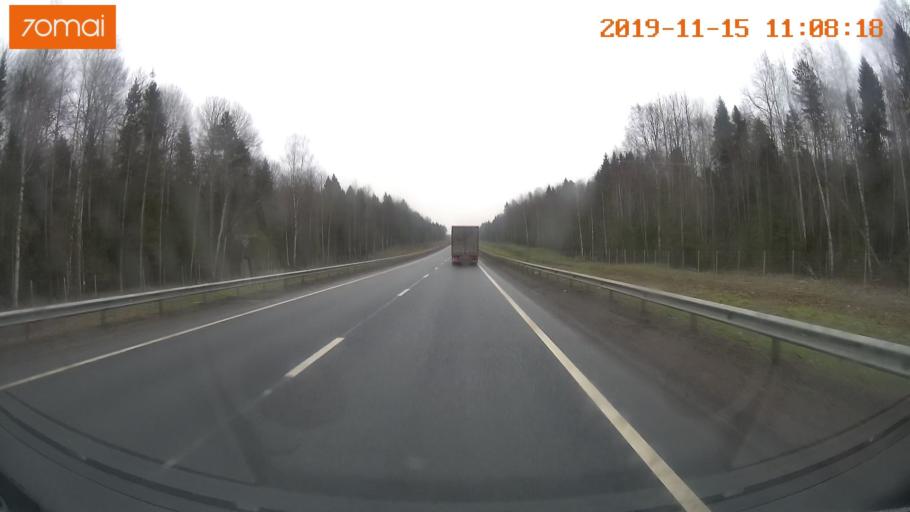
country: RU
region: Vologda
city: Chebsara
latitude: 59.1199
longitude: 39.0713
